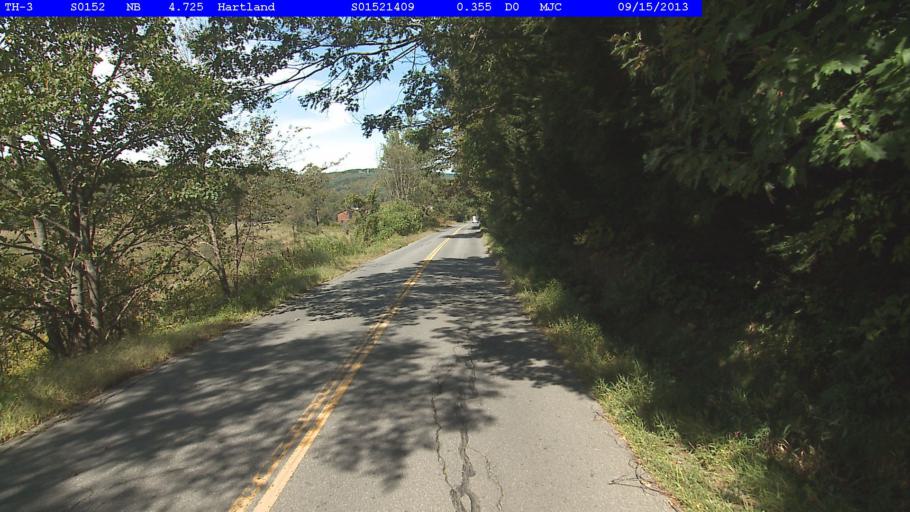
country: US
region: Vermont
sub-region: Windsor County
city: Windsor
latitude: 43.5276
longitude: -72.4370
